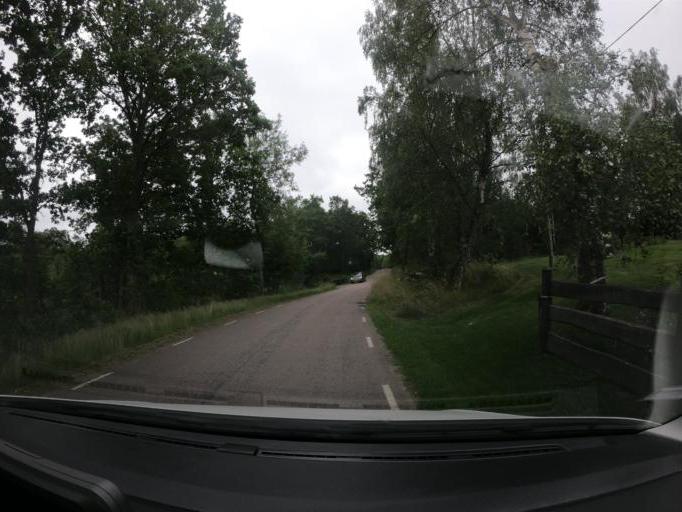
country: SE
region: Skane
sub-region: Perstorps Kommun
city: Perstorp
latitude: 56.1008
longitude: 13.3393
